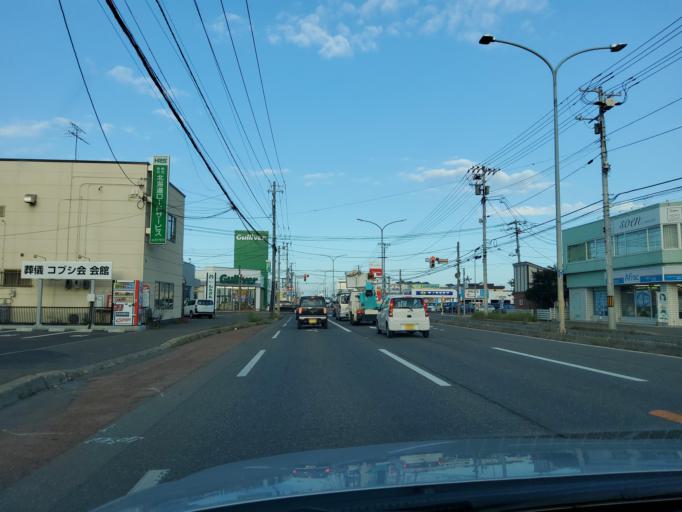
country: JP
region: Hokkaido
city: Obihiro
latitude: 42.9305
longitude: 143.1843
